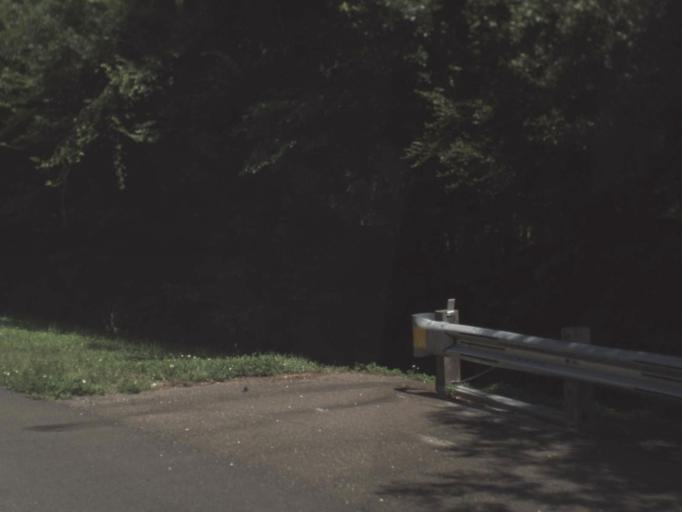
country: US
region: Florida
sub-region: Nassau County
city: Nassau Village-Ratliff
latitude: 30.5190
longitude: -81.7661
